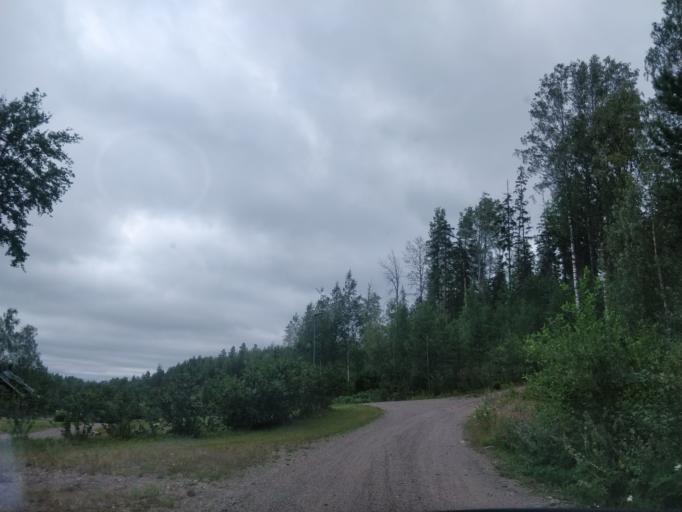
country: FI
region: Uusimaa
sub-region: Helsinki
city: Kauniainen
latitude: 60.3270
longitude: 24.7400
